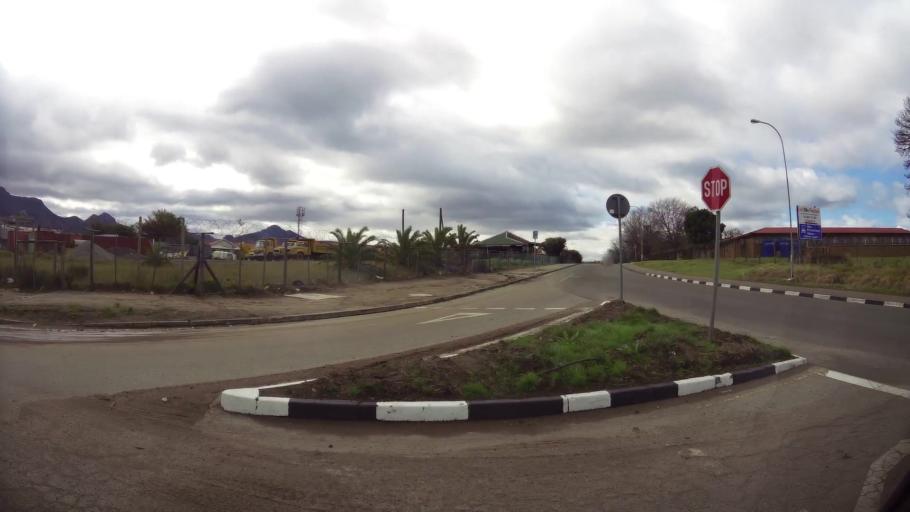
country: ZA
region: Western Cape
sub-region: Eden District Municipality
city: George
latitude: -33.9653
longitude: 22.4737
